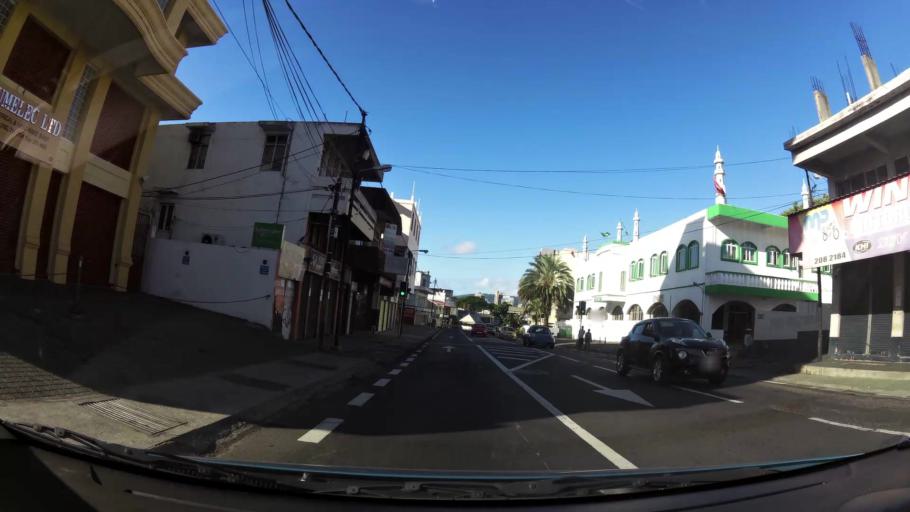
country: MU
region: Port Louis
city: Port Louis
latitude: -20.1659
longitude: 57.4903
